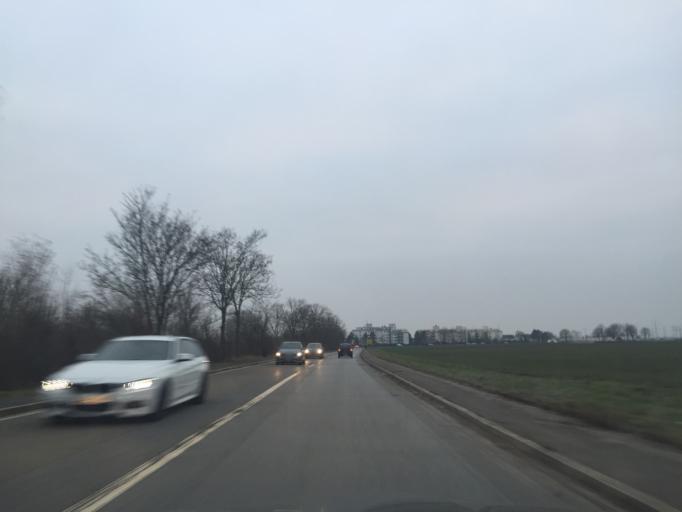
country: DE
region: Baden-Wuerttemberg
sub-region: Karlsruhe Region
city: Heddesheim
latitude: 49.5184
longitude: 8.6113
